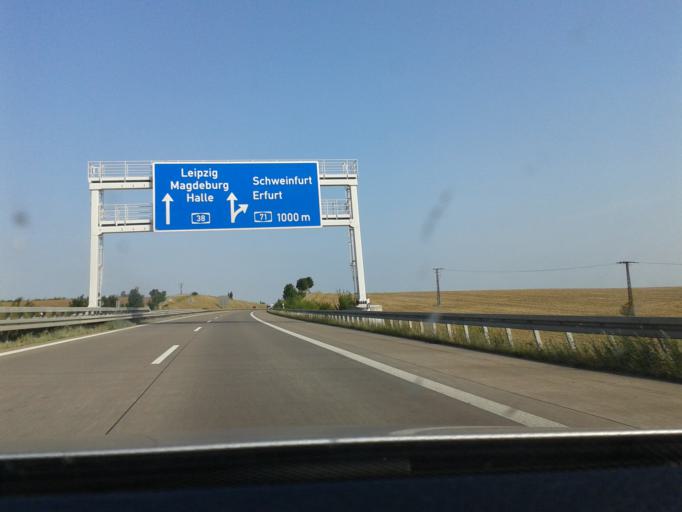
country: DE
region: Saxony-Anhalt
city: Oberroblingen
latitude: 51.4499
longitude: 11.3131
